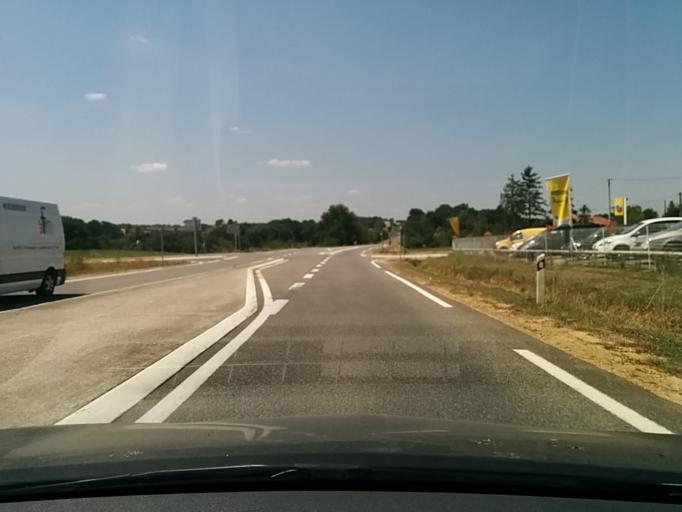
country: FR
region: Midi-Pyrenees
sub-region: Departement du Gers
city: Gimont
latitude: 43.6074
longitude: 0.9777
